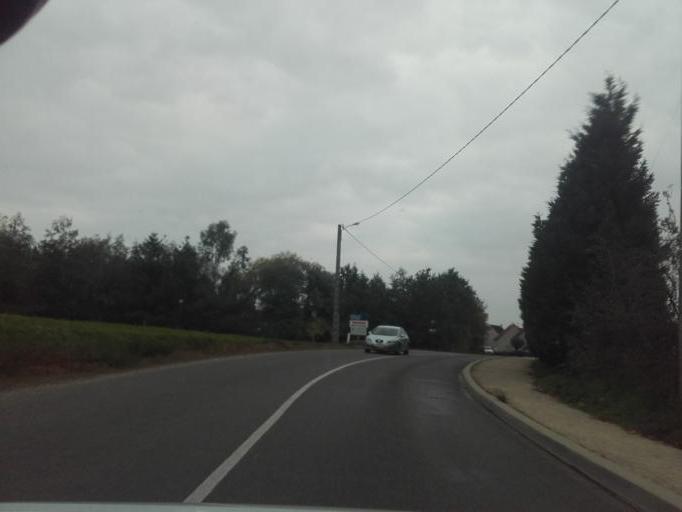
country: FR
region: Bourgogne
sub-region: Departement de Saone-et-Loire
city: Chagny
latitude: 46.9094
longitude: 4.7643
